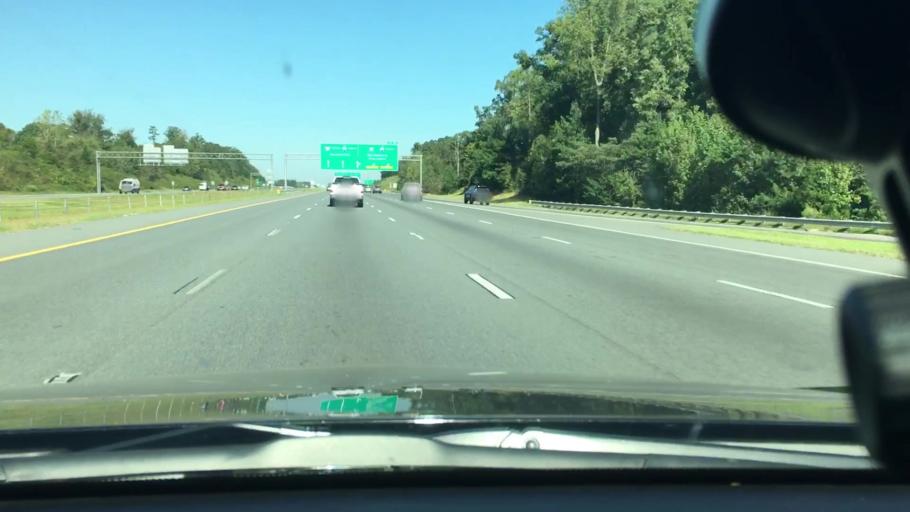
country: US
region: North Carolina
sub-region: Cabarrus County
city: Harrisburg
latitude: 35.3360
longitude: -80.7231
